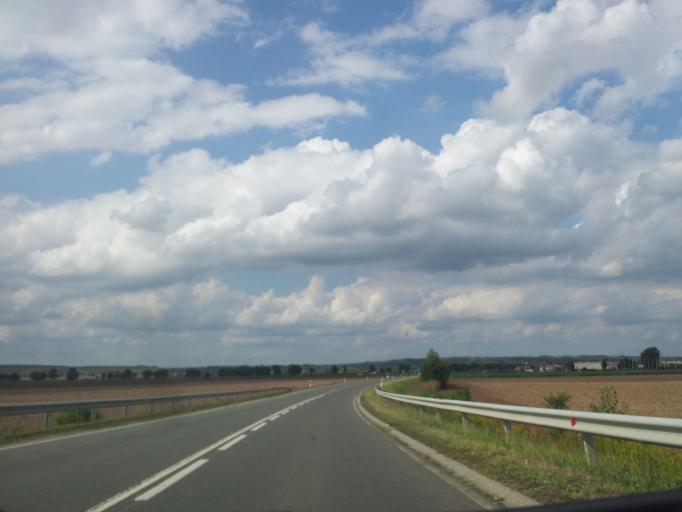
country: HU
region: Baranya
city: Mohacs
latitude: 45.9916
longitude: 18.6552
